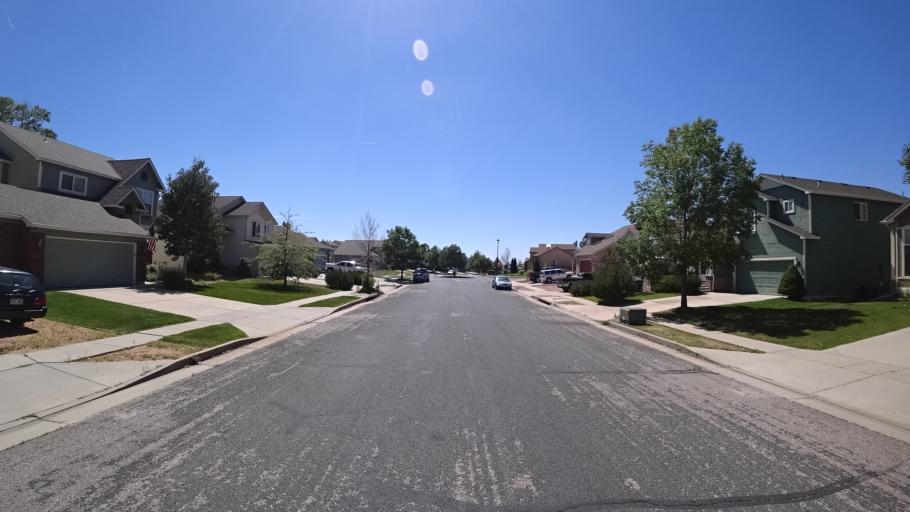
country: US
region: Colorado
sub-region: El Paso County
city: Black Forest
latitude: 38.9507
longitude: -104.7593
